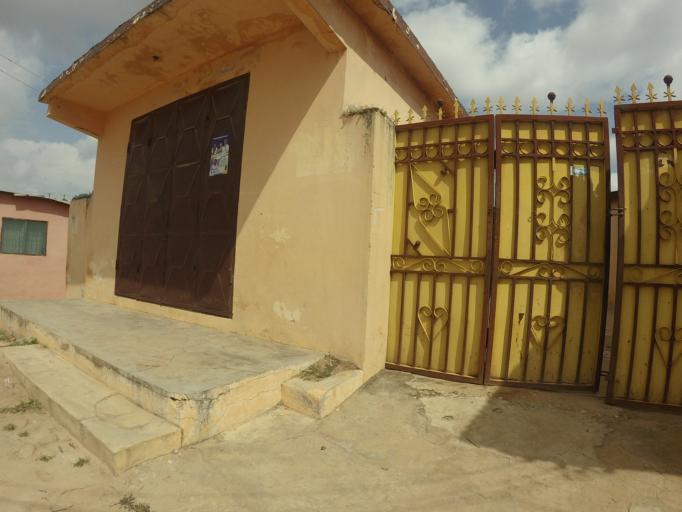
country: GH
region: Greater Accra
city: Dome
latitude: 5.6167
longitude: -0.2448
